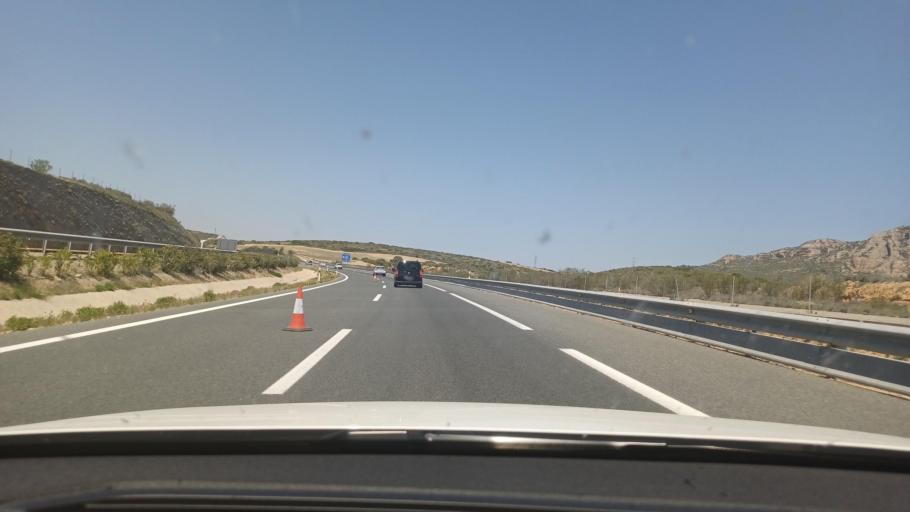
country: ES
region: Castille-La Mancha
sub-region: Provincia de Albacete
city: Almansa
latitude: 38.8774
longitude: -1.1862
